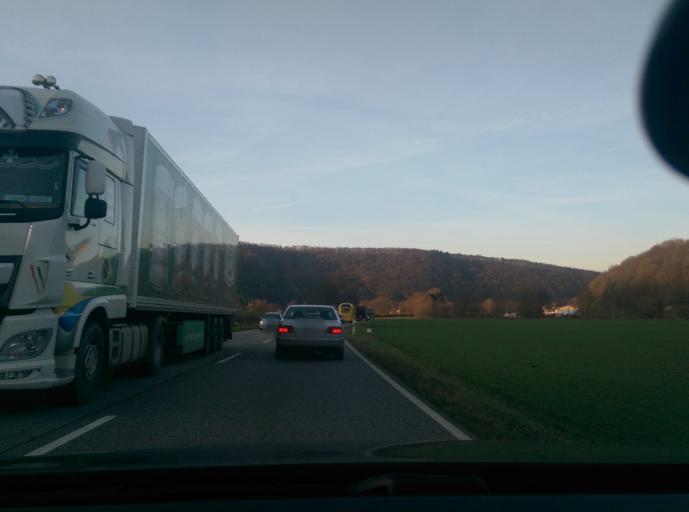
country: DE
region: Hesse
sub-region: Regierungsbezirk Kassel
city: Sontra
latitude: 51.0982
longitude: 9.9699
